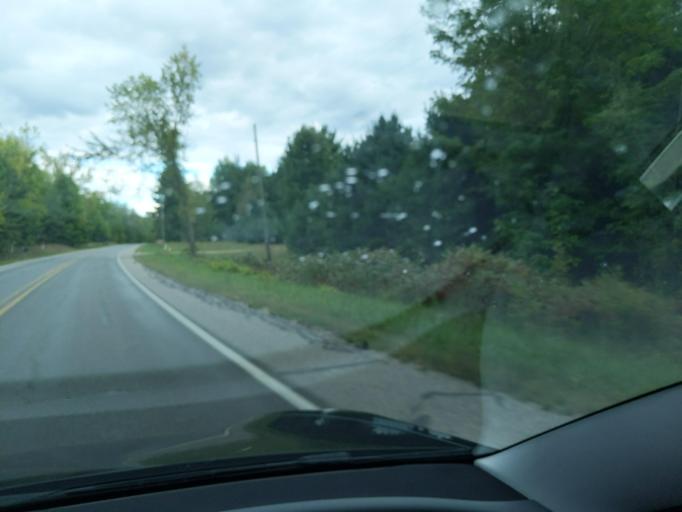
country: US
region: Michigan
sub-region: Kalkaska County
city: Rapid City
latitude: 44.8012
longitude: -85.2738
